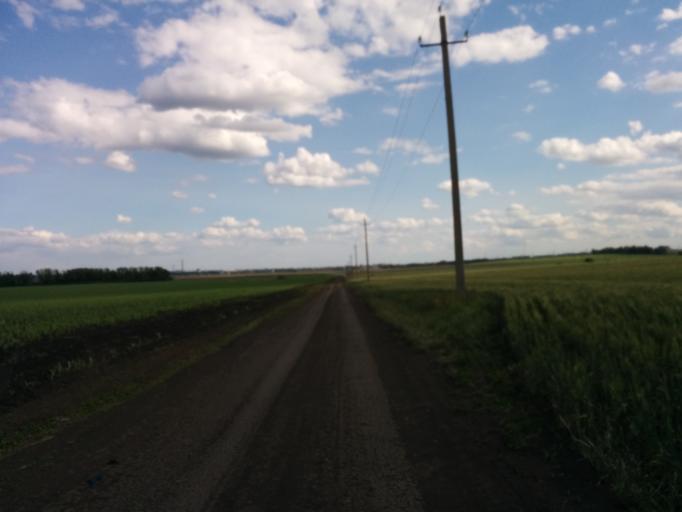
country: RU
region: Tambov
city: Donskoye
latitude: 52.7979
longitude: 41.4266
